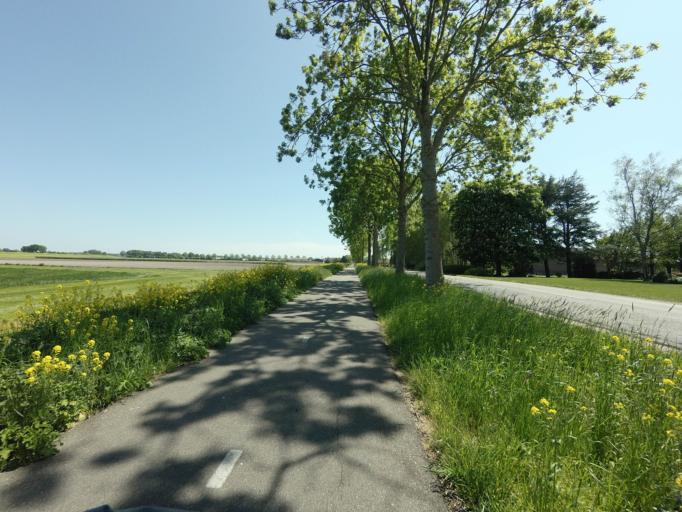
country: NL
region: North Holland
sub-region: Gemeente Uithoorn
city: Uithoorn
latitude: 52.2121
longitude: 4.8306
